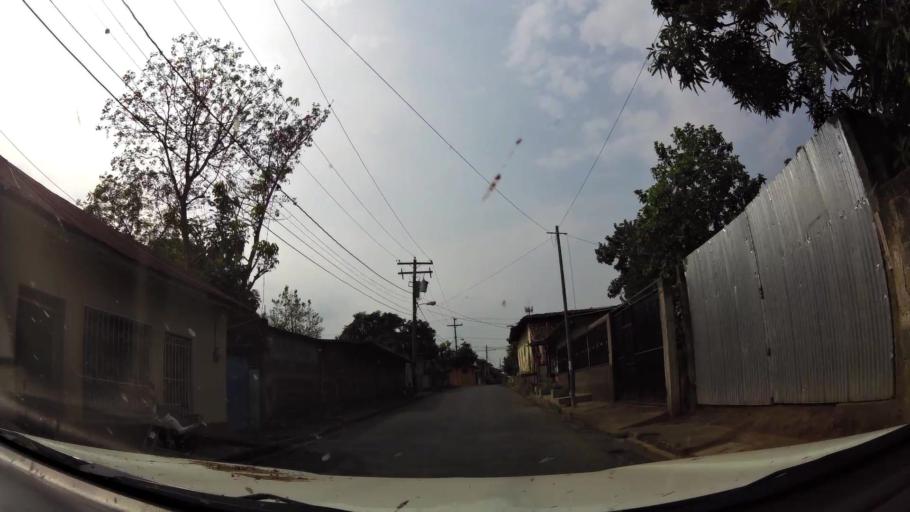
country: NI
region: Masaya
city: Masaya
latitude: 11.9724
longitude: -86.0981
